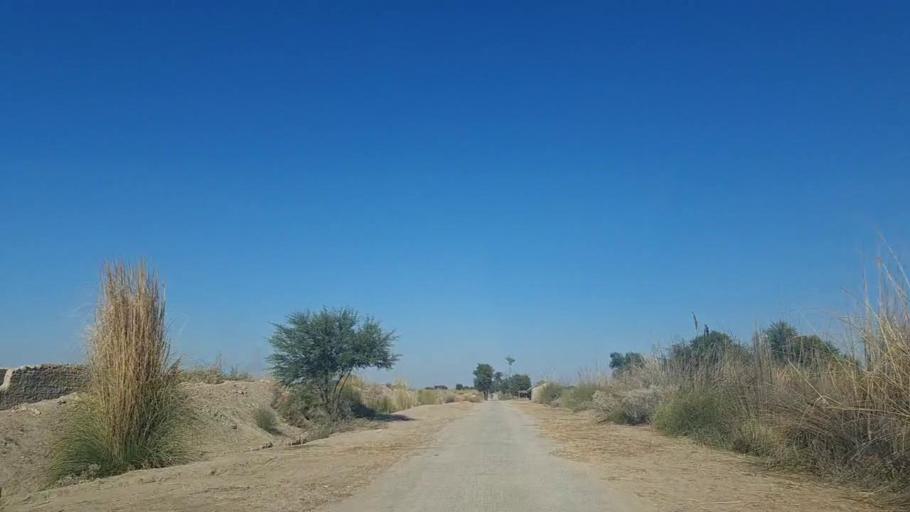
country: PK
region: Sindh
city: Khadro
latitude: 26.2106
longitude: 68.8599
